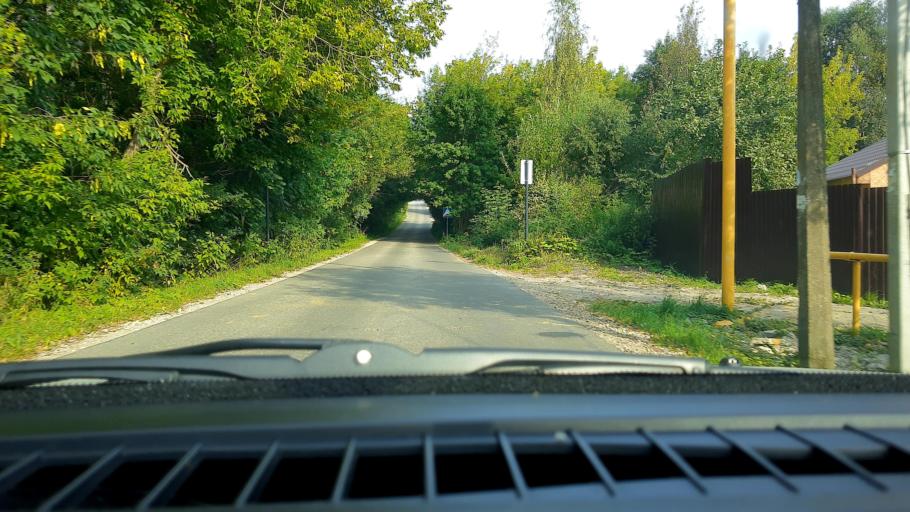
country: RU
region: Nizjnij Novgorod
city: Afonino
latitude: 56.1889
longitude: 44.0766
